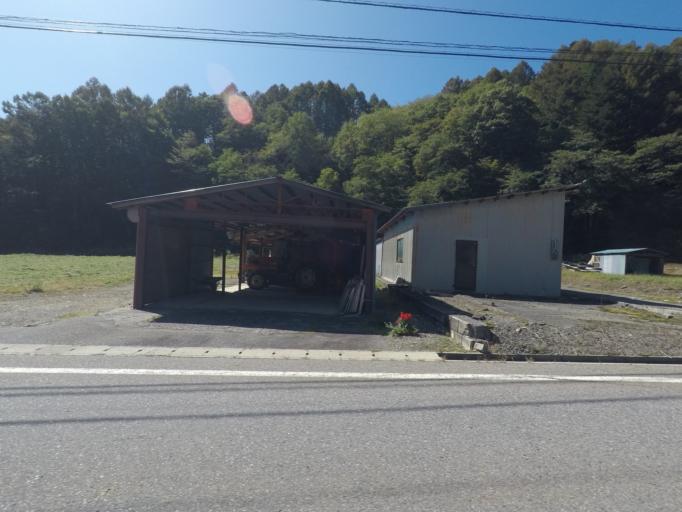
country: JP
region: Nagano
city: Shiojiri
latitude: 35.9832
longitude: 137.7427
